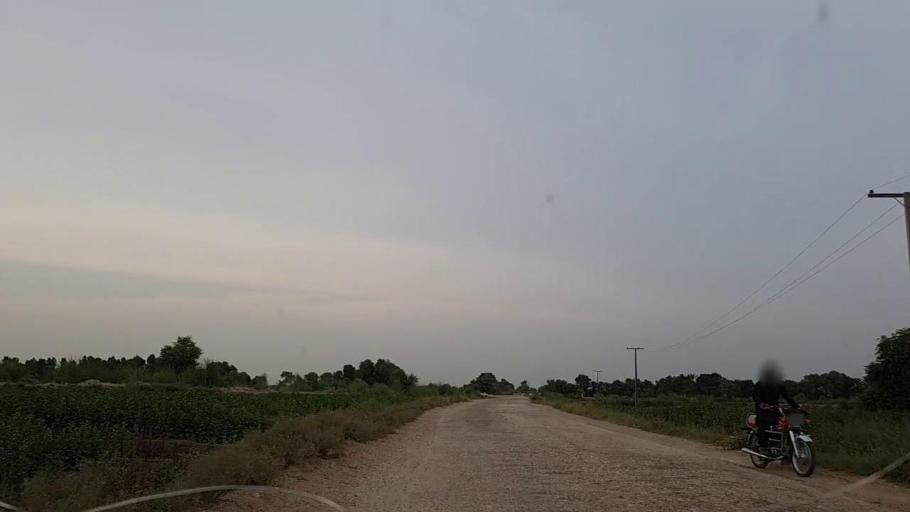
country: PK
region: Sindh
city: Mirpur Mathelo
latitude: 27.8669
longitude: 69.6331
